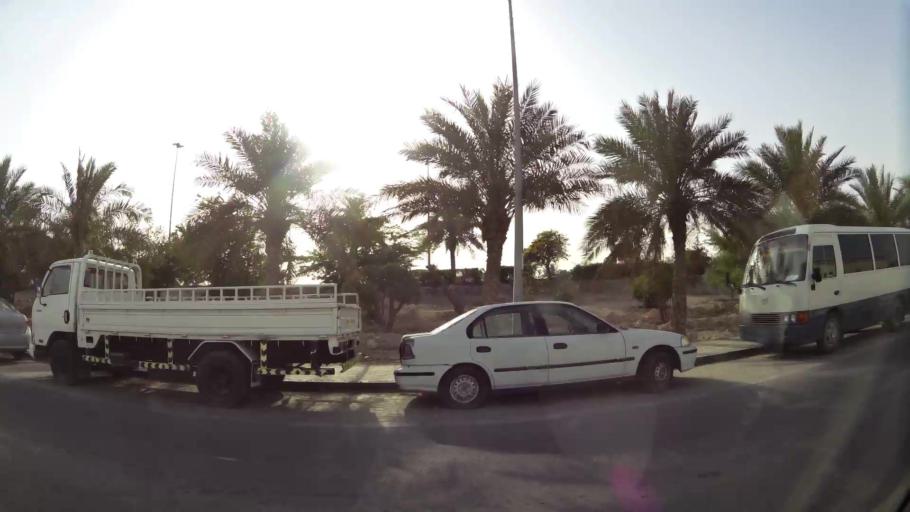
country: QA
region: Baladiyat ar Rayyan
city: Ar Rayyan
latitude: 25.2288
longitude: 51.4319
